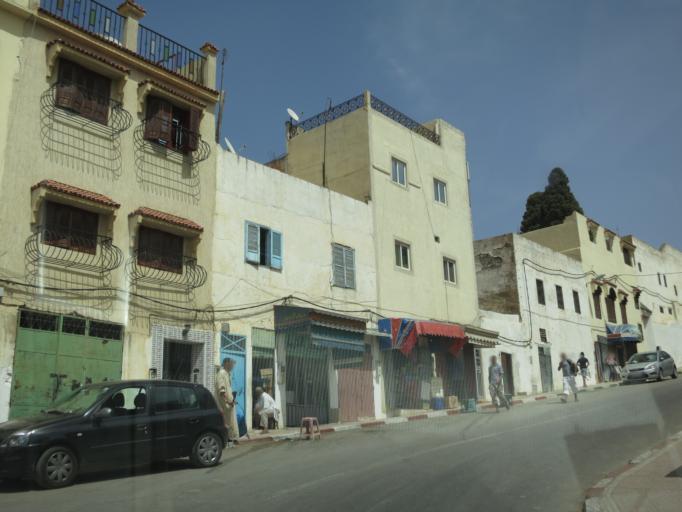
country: MA
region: Meknes-Tafilalet
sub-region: Meknes
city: Meknes
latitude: 34.0570
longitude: -5.5226
